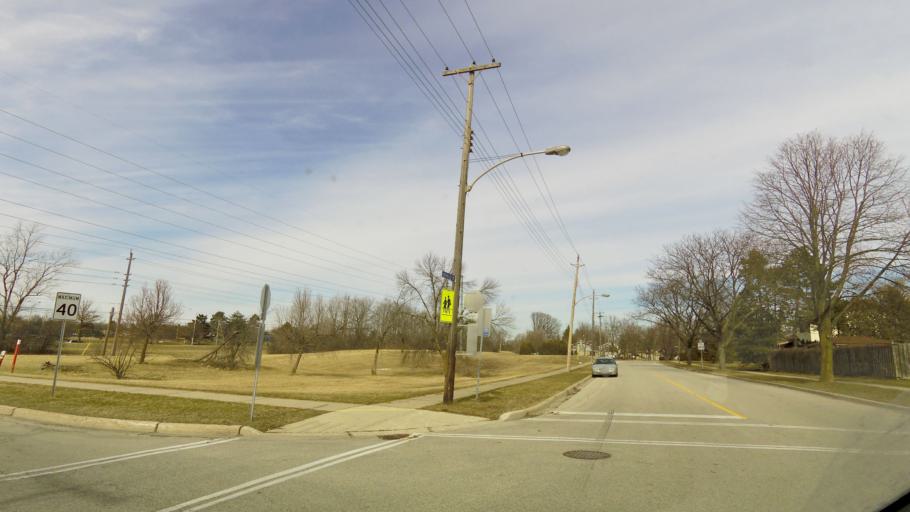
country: CA
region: Ontario
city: Burlington
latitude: 43.3600
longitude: -79.8254
